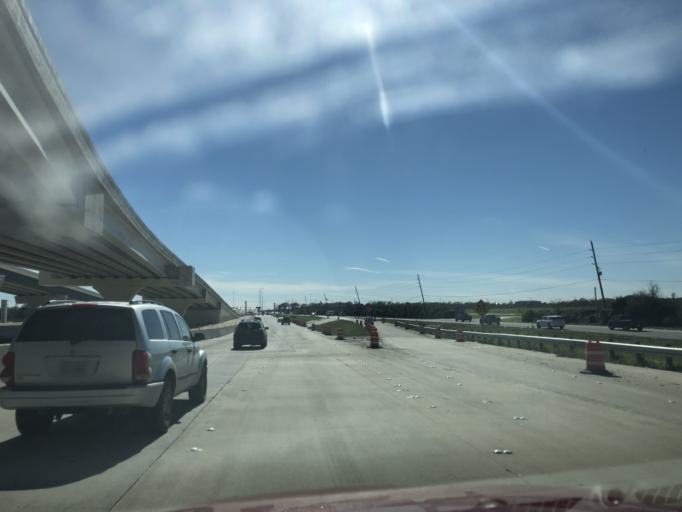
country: US
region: Texas
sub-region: Brazoria County
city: Brookside Village
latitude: 29.5943
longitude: -95.3869
